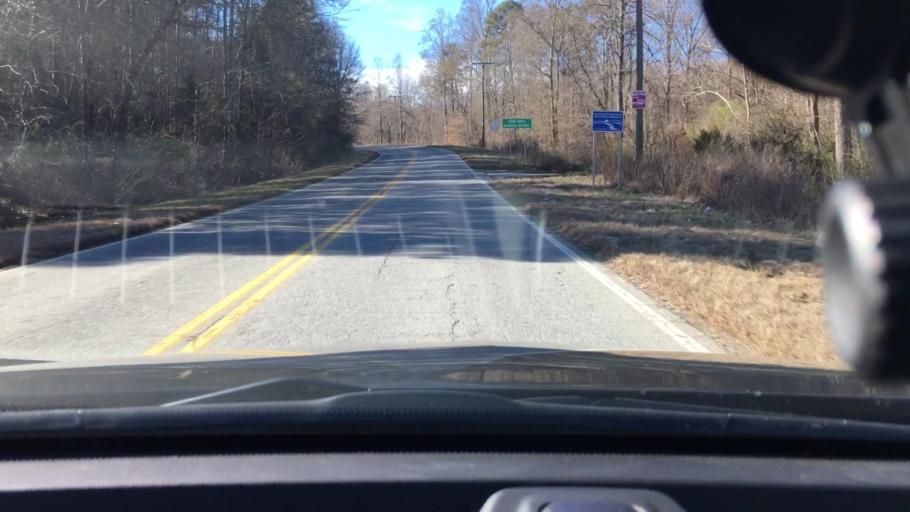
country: US
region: South Carolina
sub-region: Spartanburg County
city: Pacolet
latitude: 34.9313
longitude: -81.7346
